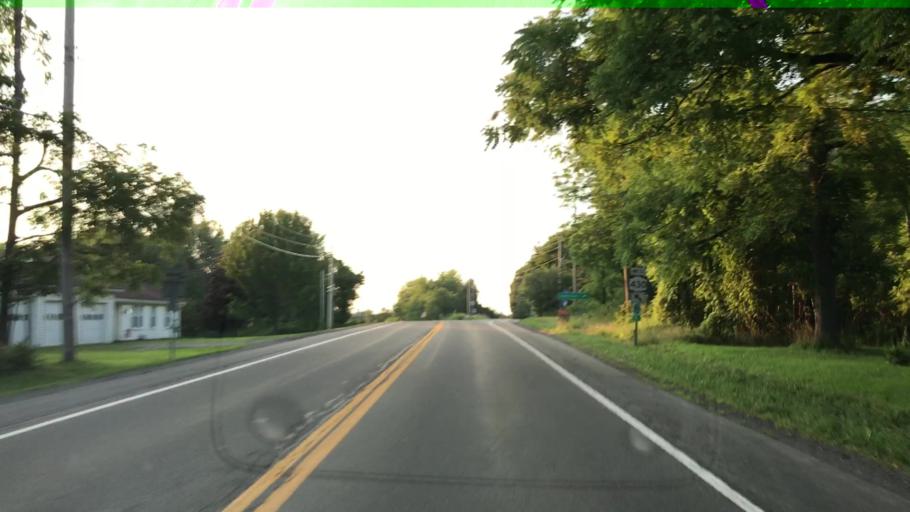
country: US
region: New York
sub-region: Chautauqua County
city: Mayville
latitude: 42.2577
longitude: -79.4682
